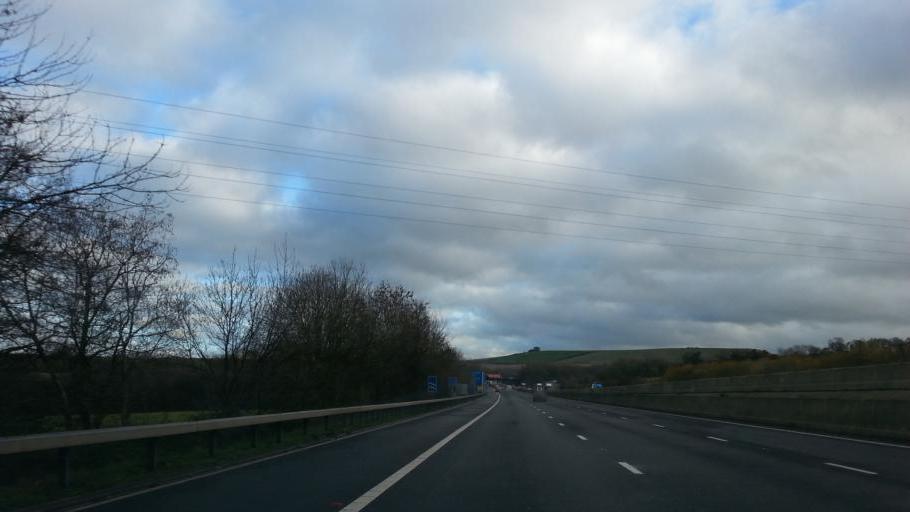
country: GB
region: England
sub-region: Borough of Swindon
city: Chiseldon
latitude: 51.5286
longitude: -1.7370
